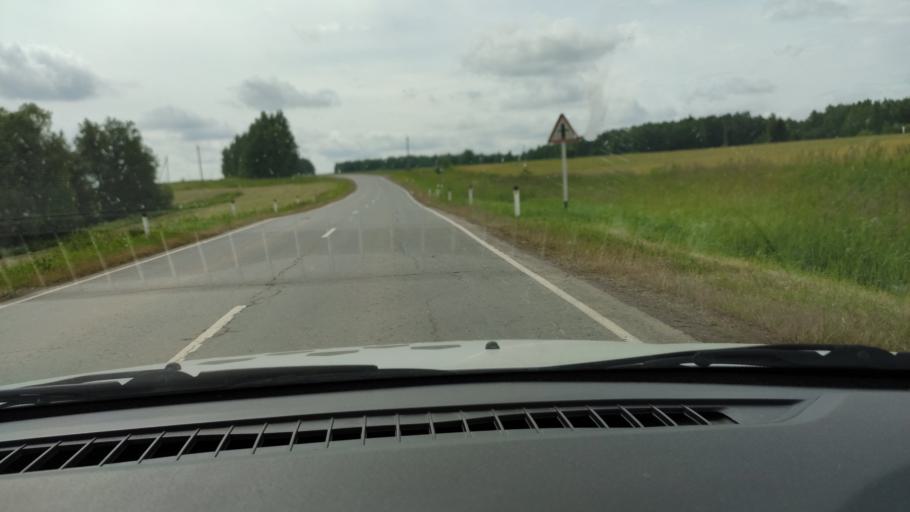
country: RU
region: Perm
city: Kukushtan
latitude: 57.4786
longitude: 56.5821
